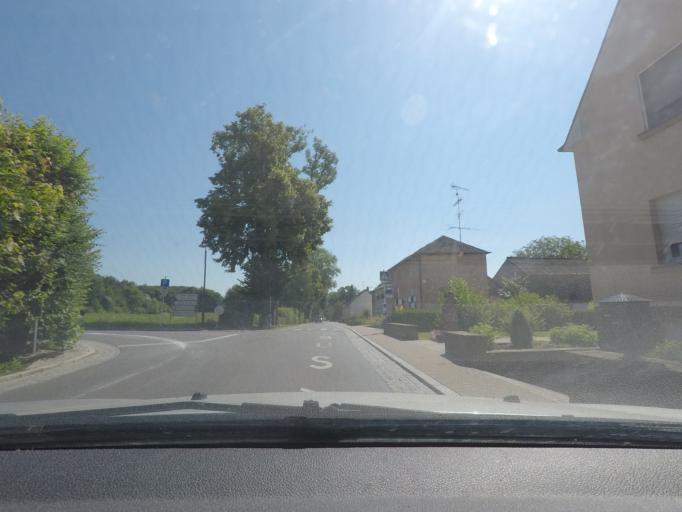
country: LU
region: Diekirch
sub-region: Canton de Redange
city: Redange-sur-Attert
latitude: 49.7659
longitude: 5.8955
